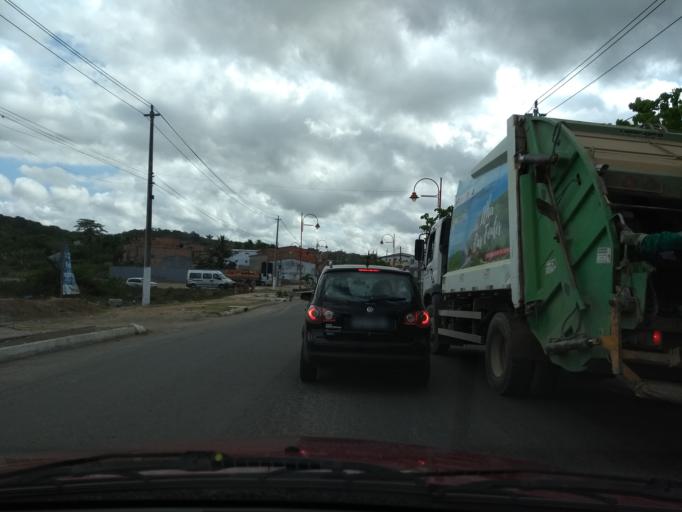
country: BR
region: Bahia
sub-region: Sao Francisco Do Conde
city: Sao Francisco do Conde
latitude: -12.6186
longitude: -38.6685
